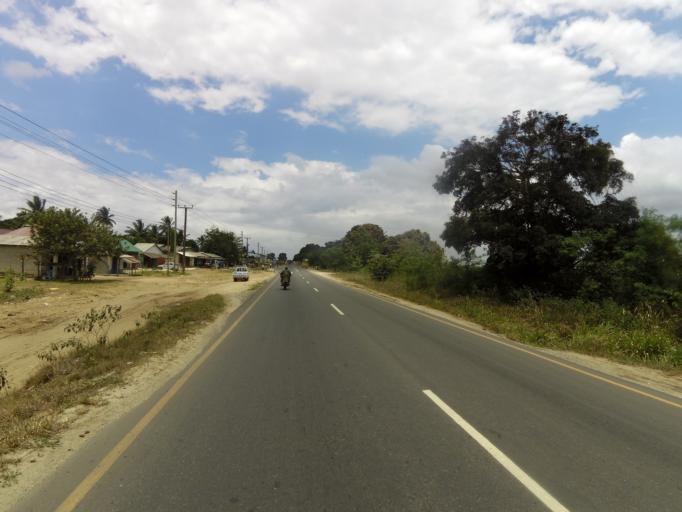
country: TZ
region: Pwani
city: Vikindu
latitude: -6.9816
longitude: 39.2919
